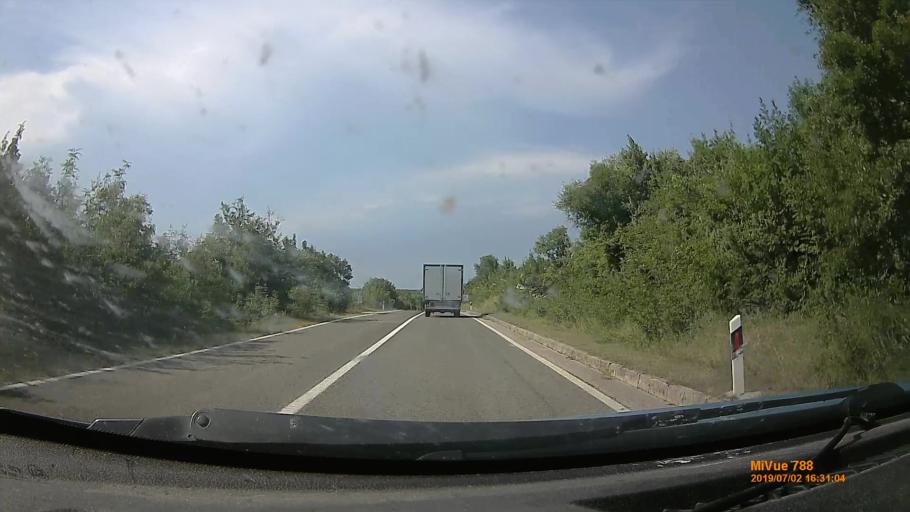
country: HR
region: Primorsko-Goranska
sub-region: Grad Krk
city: Krk
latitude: 45.0496
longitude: 14.4884
